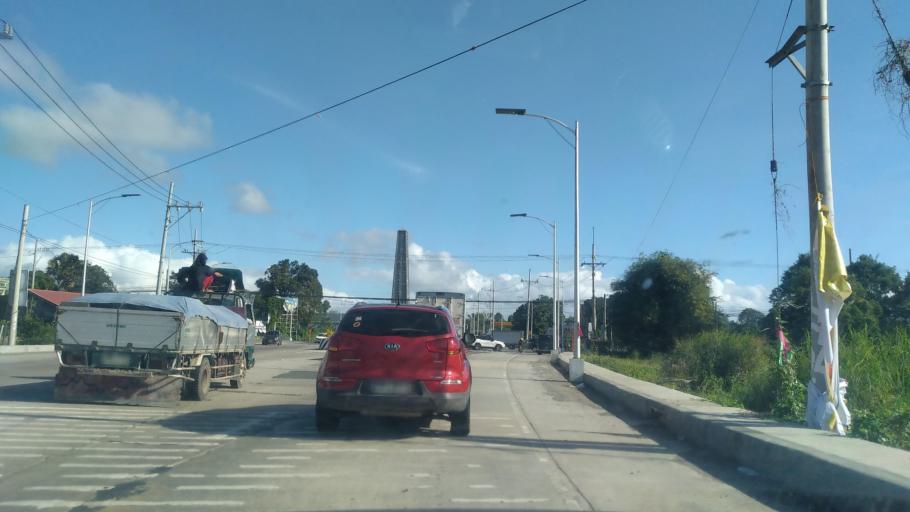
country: PH
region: Calabarzon
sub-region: Province of Quezon
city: Isabang
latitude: 13.9509
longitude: 121.5773
